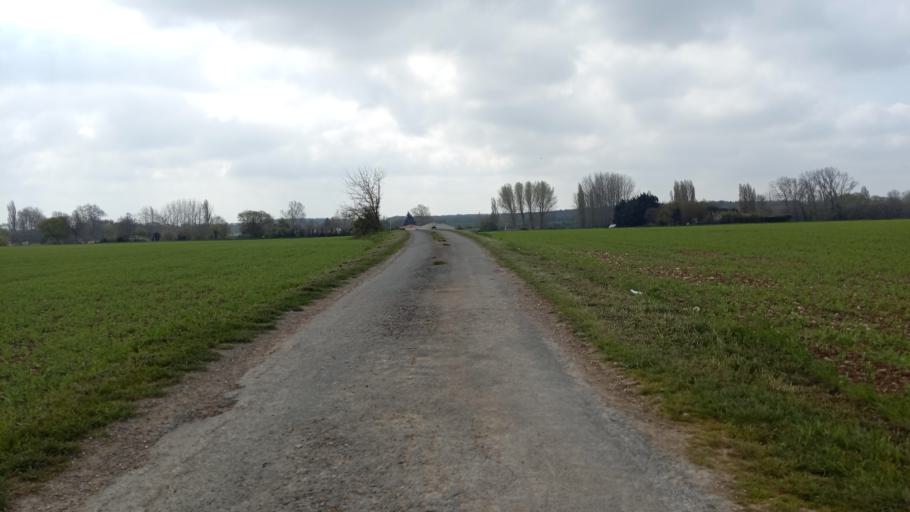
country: FR
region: Poitou-Charentes
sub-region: Departement de la Charente-Maritime
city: Verines
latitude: 46.1573
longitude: -0.9344
